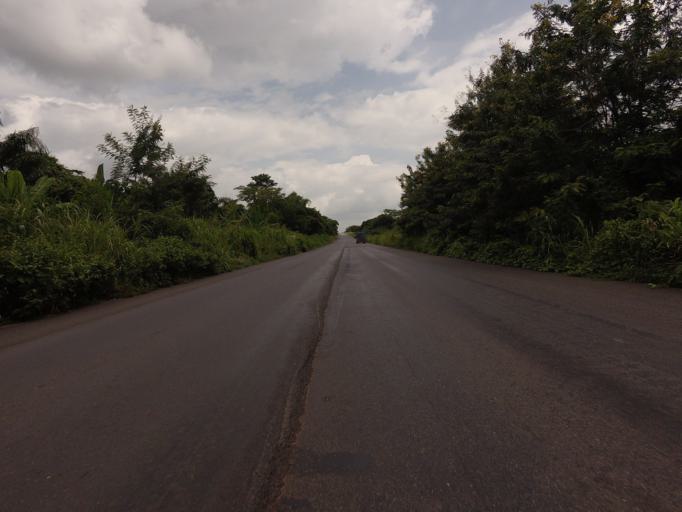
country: GH
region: Volta
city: Ho
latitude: 6.5607
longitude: 0.2640
